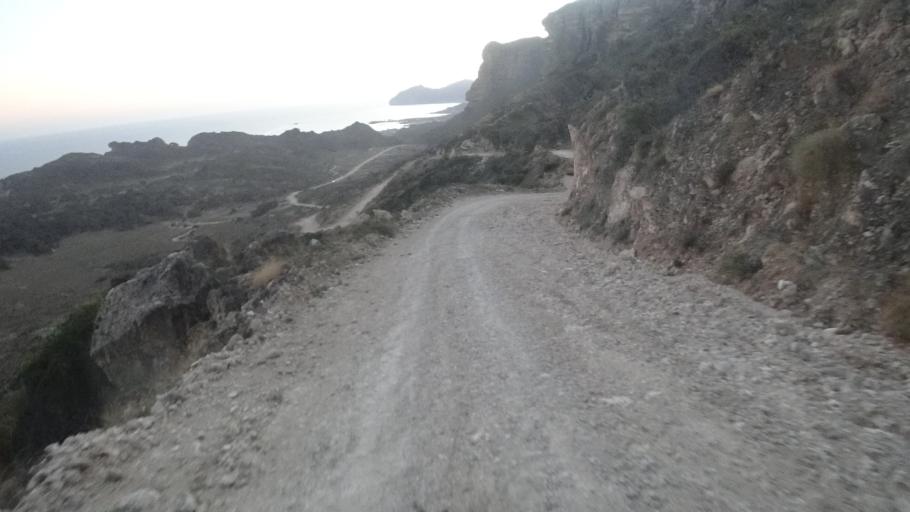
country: OM
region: Zufar
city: Salalah
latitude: 16.8571
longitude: 53.7329
